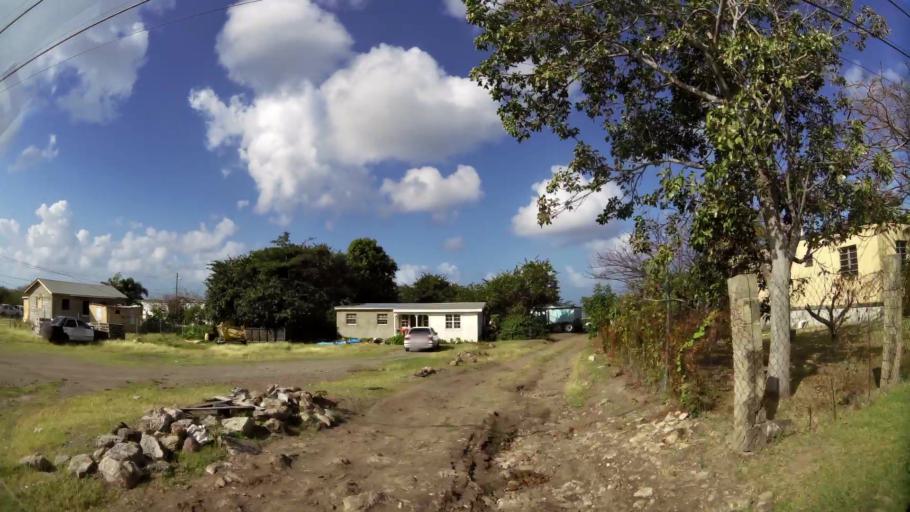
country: KN
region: Saint Paul Charlestown
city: Charlestown
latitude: 17.1268
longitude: -62.6267
